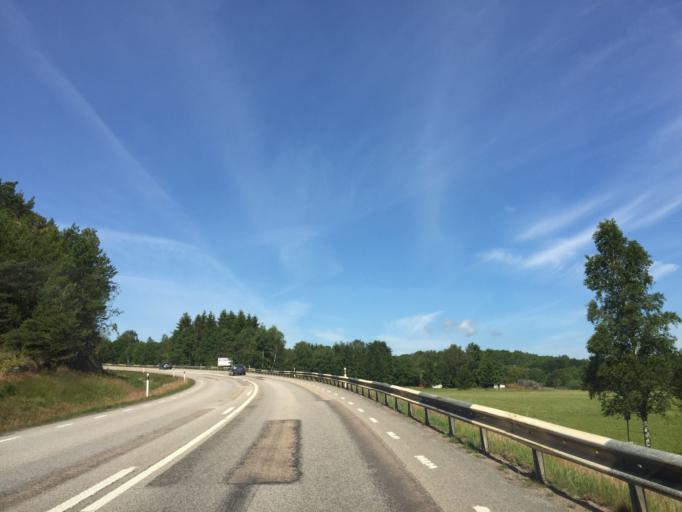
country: SE
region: Vaestra Goetaland
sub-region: Lysekils Kommun
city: Lysekil
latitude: 58.3060
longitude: 11.4891
